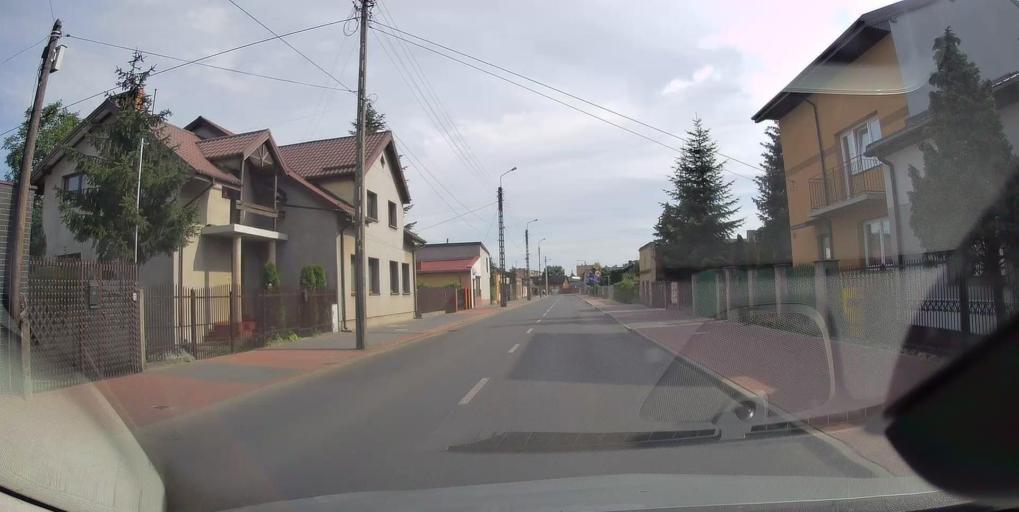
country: PL
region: Lodz Voivodeship
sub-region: Powiat tomaszowski
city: Tomaszow Mazowiecki
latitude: 51.5267
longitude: 19.9974
